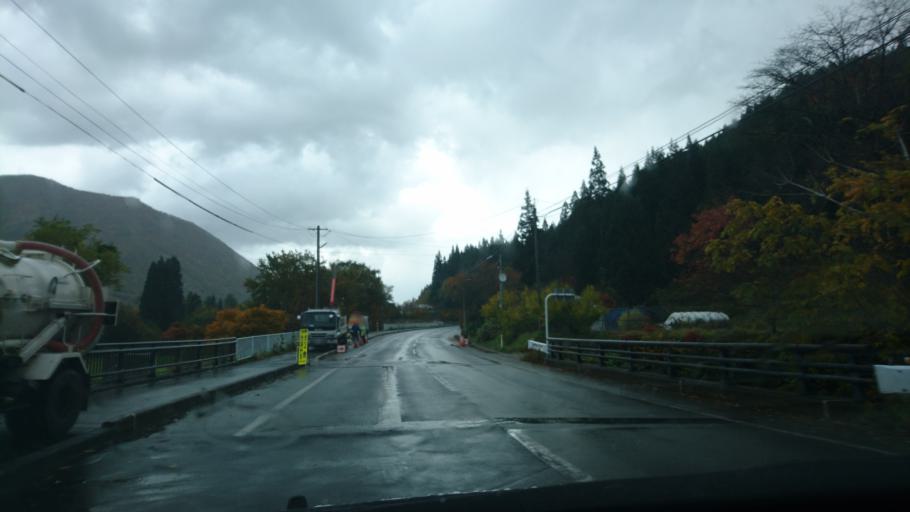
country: JP
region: Iwate
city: Shizukuishi
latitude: 39.5962
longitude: 140.9218
